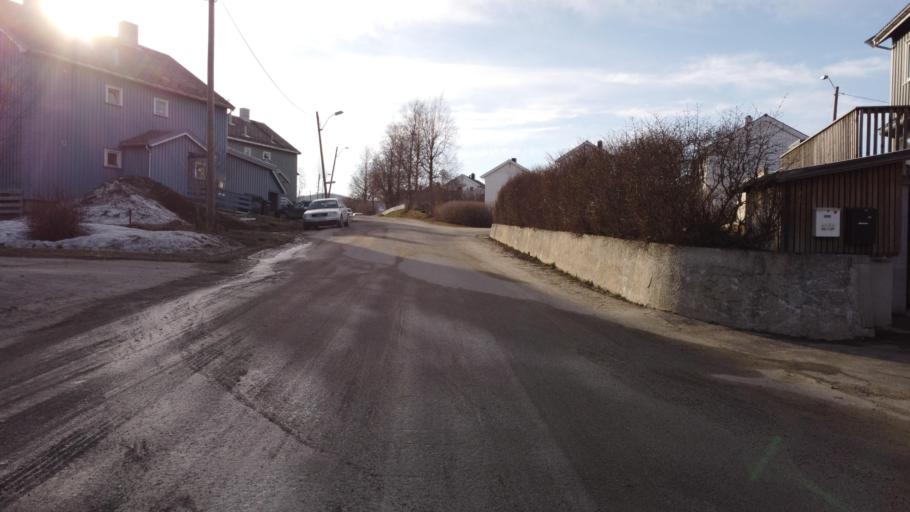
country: NO
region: Nordland
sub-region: Rana
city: Mo i Rana
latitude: 66.3145
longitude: 14.1457
